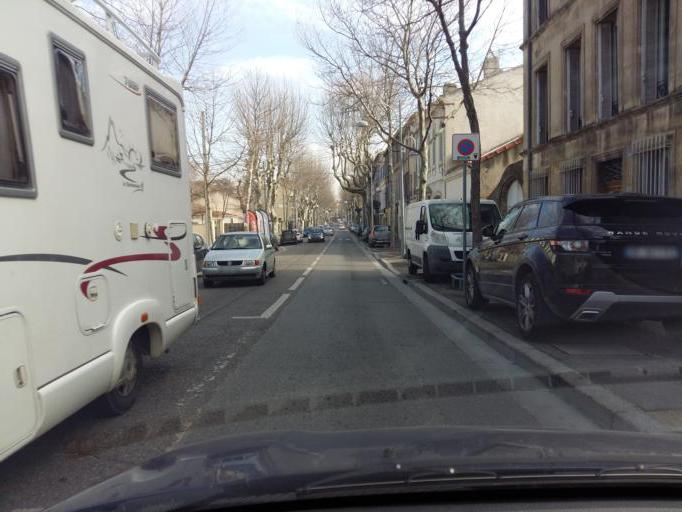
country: FR
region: Provence-Alpes-Cote d'Azur
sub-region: Departement des Bouches-du-Rhone
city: Salon-de-Provence
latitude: 43.6406
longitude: 5.0906
